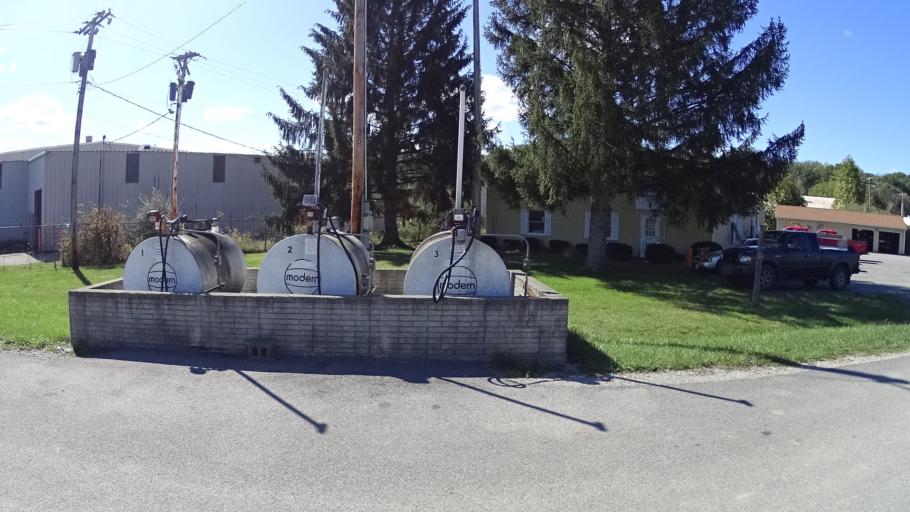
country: US
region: Ohio
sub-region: Lorain County
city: Grafton
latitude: 41.2761
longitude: -82.0650
